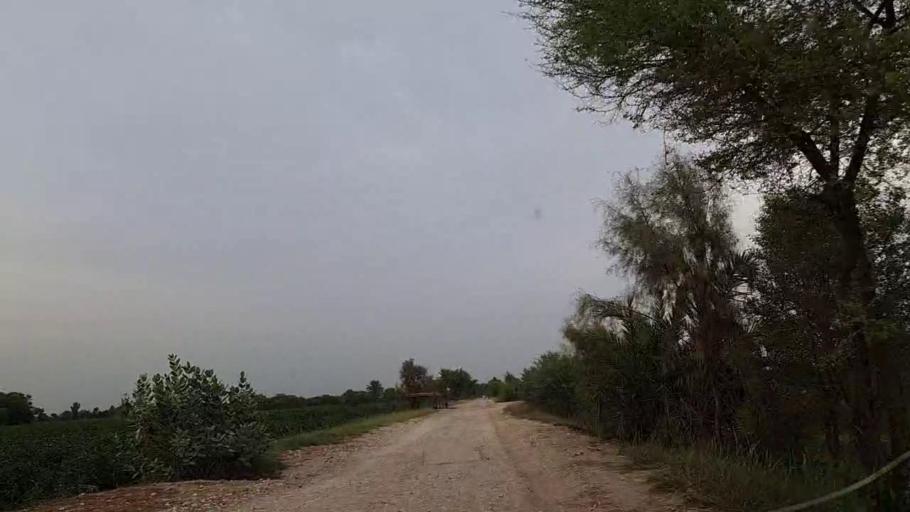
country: PK
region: Sindh
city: Mirpur Mathelo
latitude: 27.8423
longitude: 69.6231
